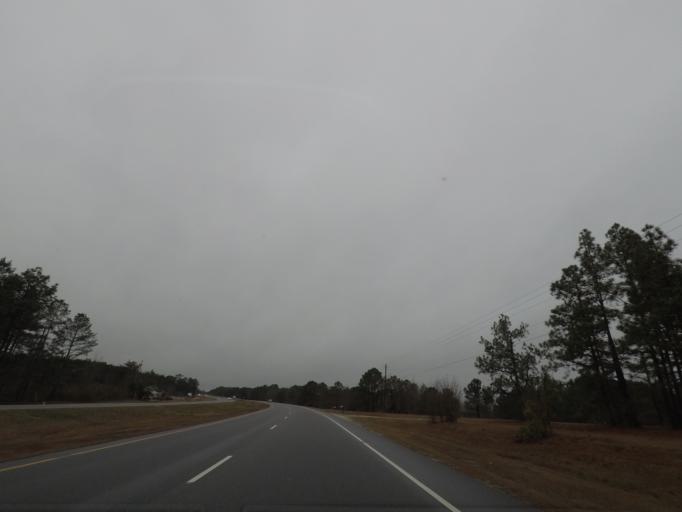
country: US
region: North Carolina
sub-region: Lee County
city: Broadway
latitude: 35.3354
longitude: -79.0954
